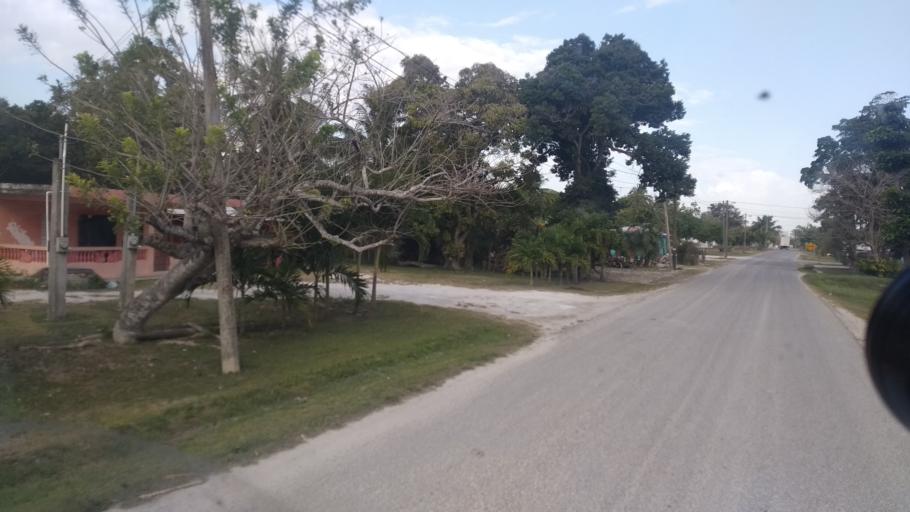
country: BZ
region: Corozal
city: Corozal
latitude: 18.3044
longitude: -88.5188
